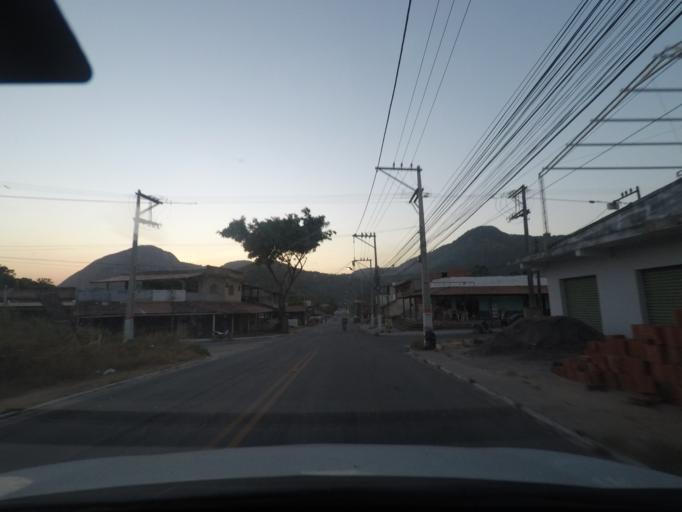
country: BR
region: Rio de Janeiro
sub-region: Niteroi
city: Niteroi
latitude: -22.9620
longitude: -42.9990
